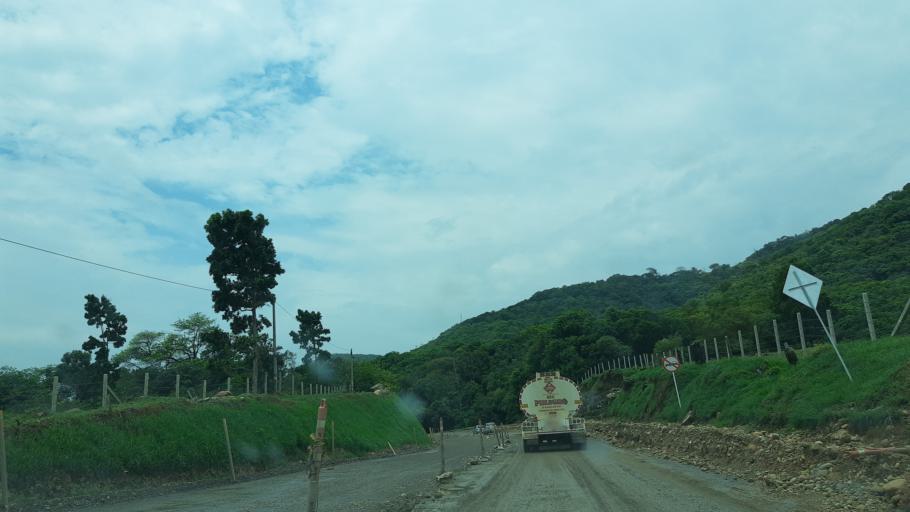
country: CO
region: Casanare
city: Sabanalarga
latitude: 4.7631
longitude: -73.0081
